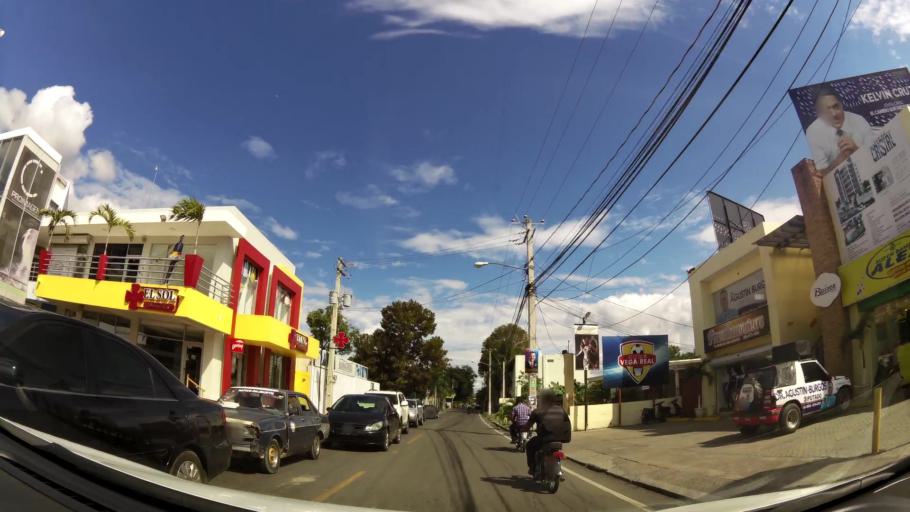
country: DO
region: La Vega
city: Concepcion de La Vega
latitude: 19.2206
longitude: -70.5234
